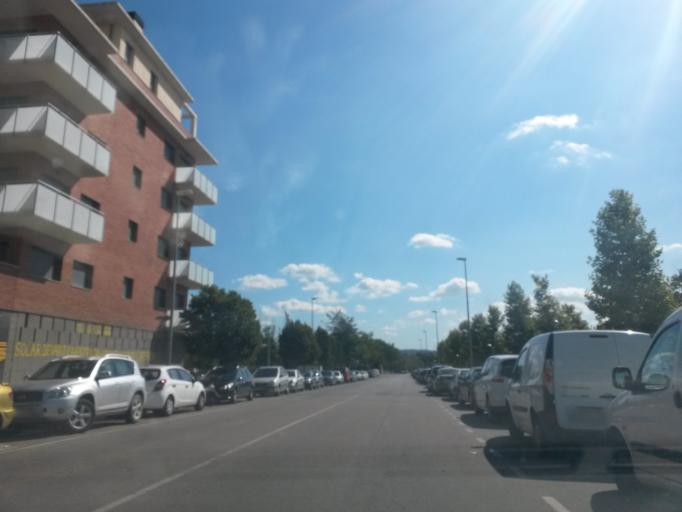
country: ES
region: Catalonia
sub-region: Provincia de Girona
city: Salt
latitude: 41.9707
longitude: 2.8004
